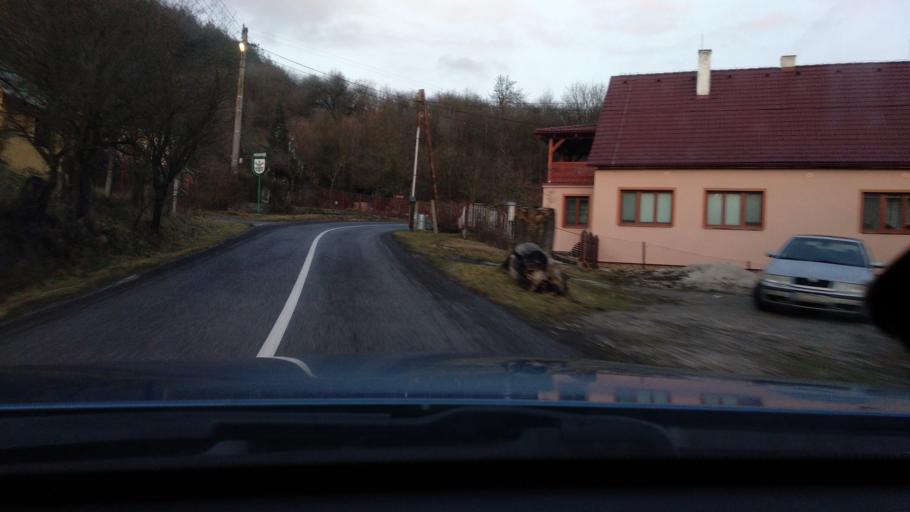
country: SK
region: Nitriansky
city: Banovce nad Bebravou
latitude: 48.8565
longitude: 18.2997
